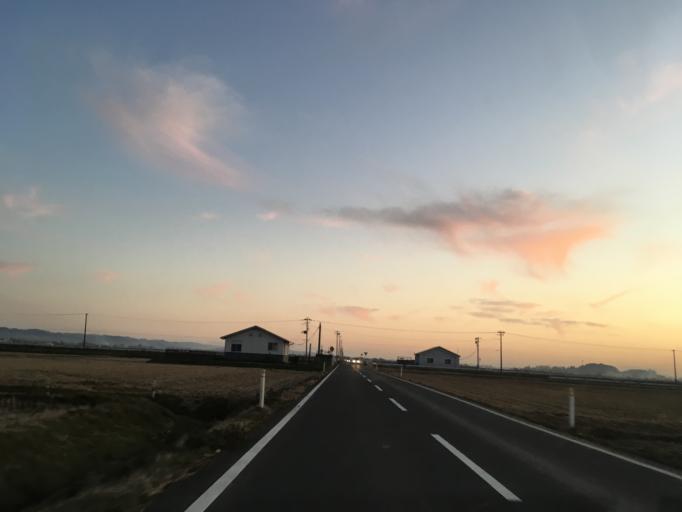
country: JP
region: Iwate
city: Ichinoseki
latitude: 38.7471
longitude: 141.2373
